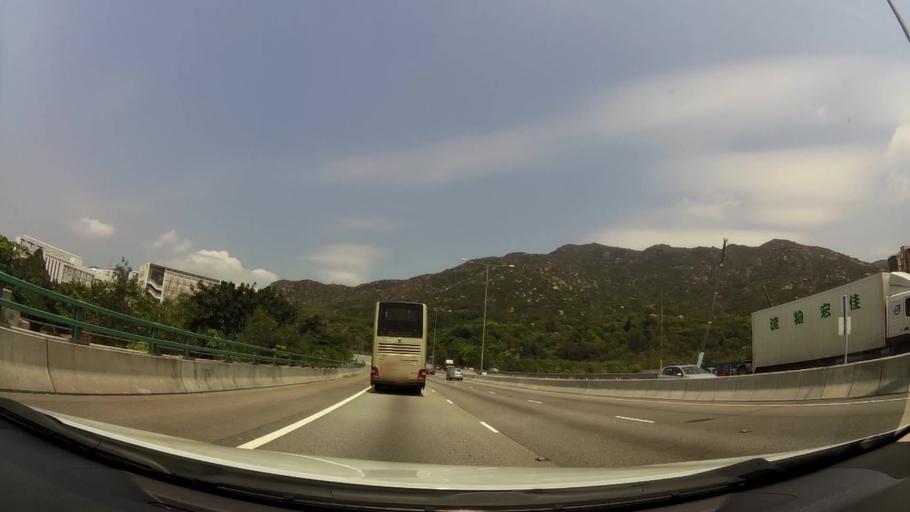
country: HK
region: Tuen Mun
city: Tuen Mun
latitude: 22.3736
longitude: 113.9975
